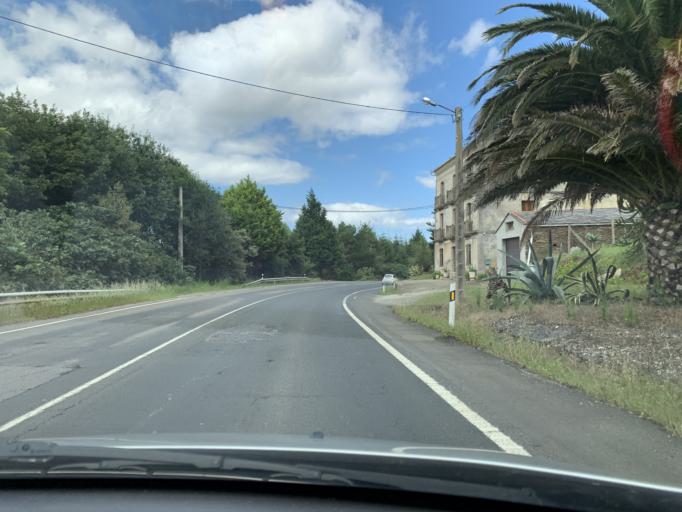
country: ES
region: Galicia
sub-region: Provincia de Lugo
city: Barreiros
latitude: 43.5268
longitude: -7.2666
